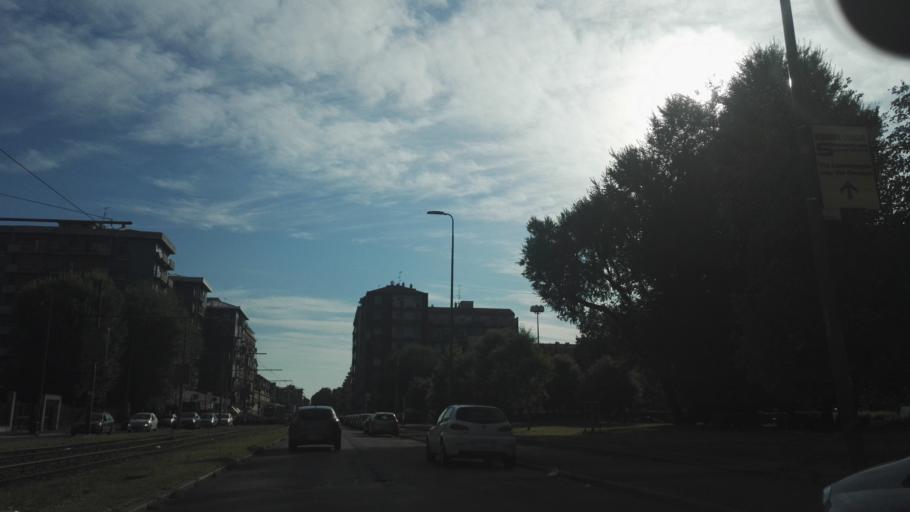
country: IT
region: Lombardy
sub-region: Citta metropolitana di Milano
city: Romano Banco
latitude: 45.4469
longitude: 9.1367
